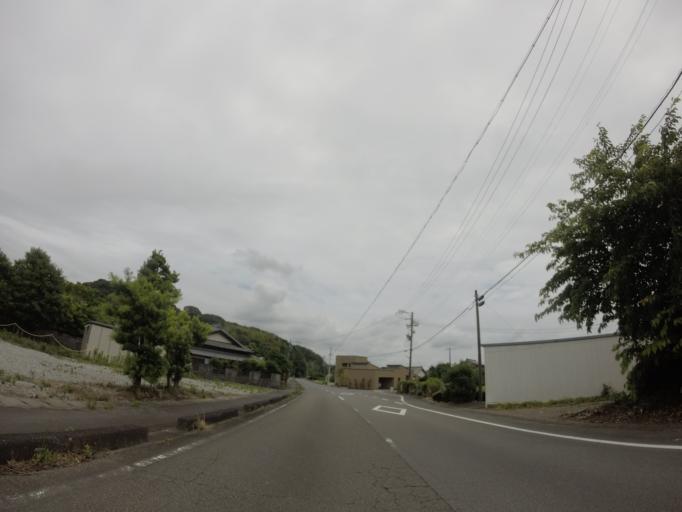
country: JP
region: Shizuoka
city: Shimada
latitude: 34.7788
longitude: 138.1709
